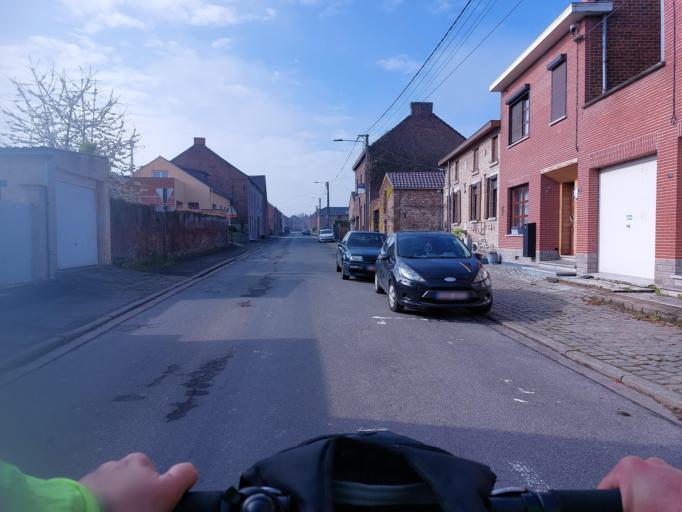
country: BE
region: Wallonia
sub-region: Province du Hainaut
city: Estinnes-au-Val
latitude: 50.4316
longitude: 4.0407
